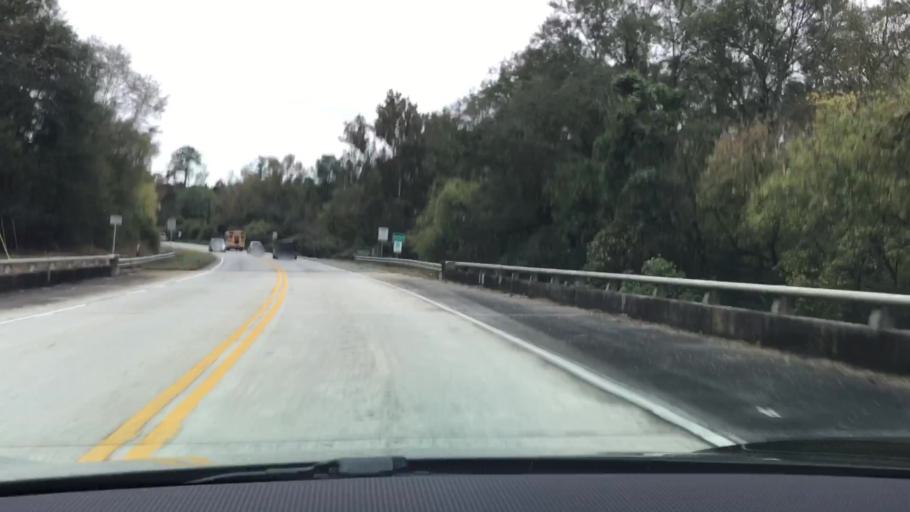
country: US
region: Georgia
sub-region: Greene County
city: Greensboro
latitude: 33.5876
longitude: -83.1939
